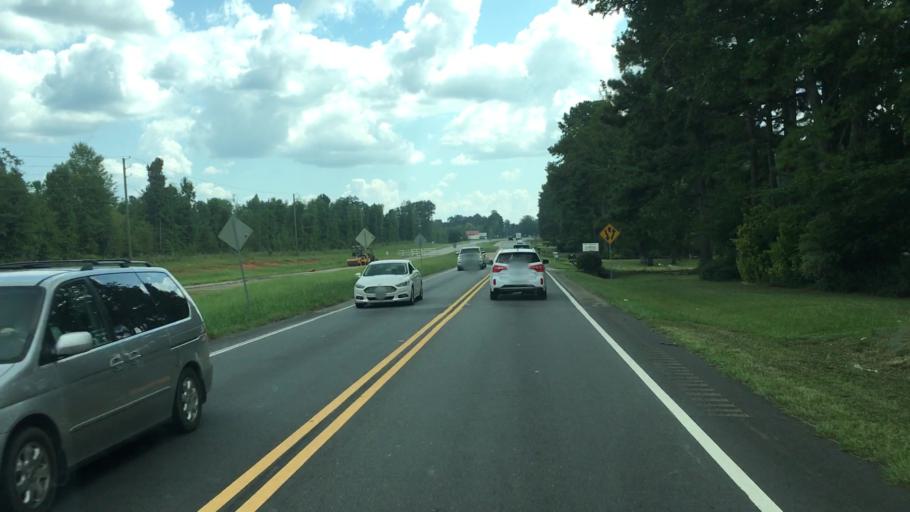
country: US
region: Georgia
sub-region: Putnam County
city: Eatonton
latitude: 33.3542
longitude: -83.3905
